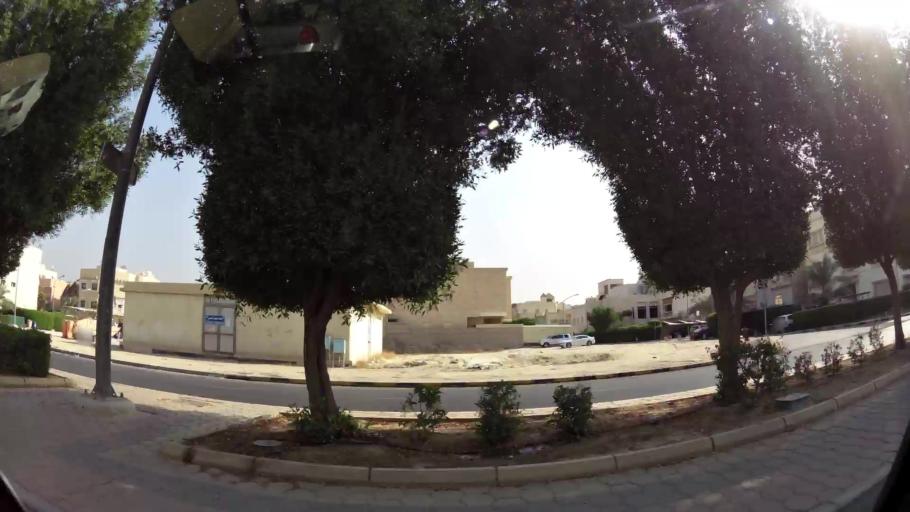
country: KW
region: Mubarak al Kabir
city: Sabah as Salim
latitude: 29.2763
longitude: 48.0411
